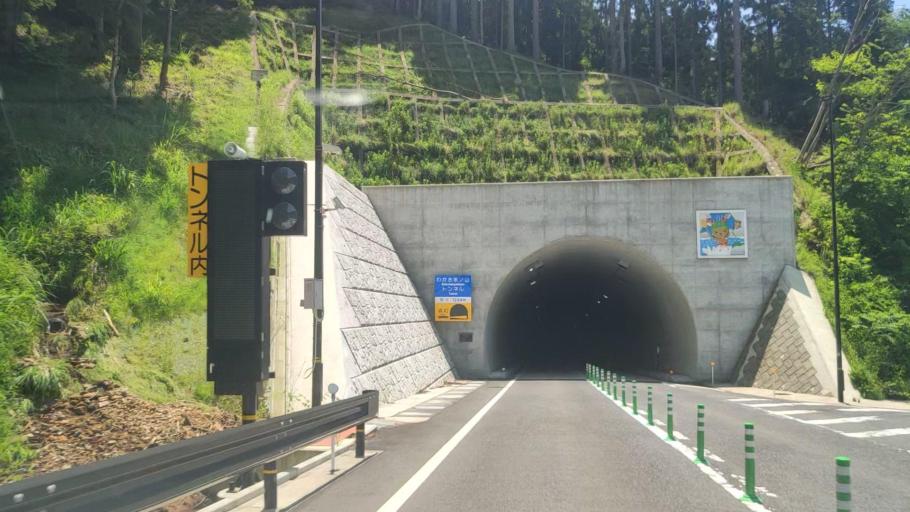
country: JP
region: Tottori
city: Tottori
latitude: 35.3550
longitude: 134.4731
